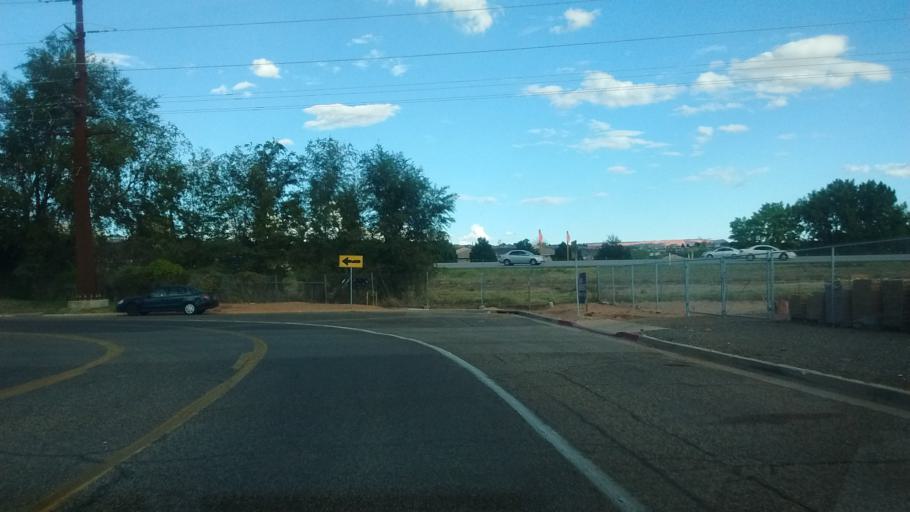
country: US
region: Utah
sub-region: Washington County
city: Saint George
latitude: 37.1013
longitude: -113.5625
